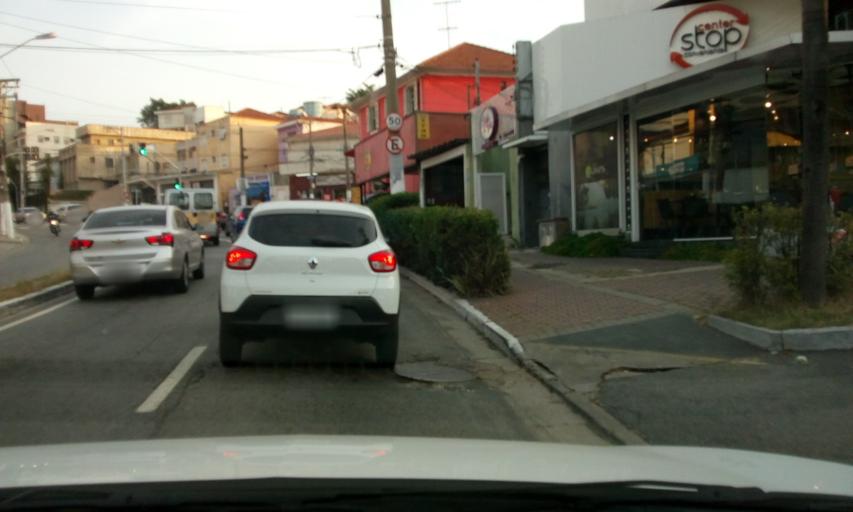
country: BR
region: Sao Paulo
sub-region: Sao Paulo
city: Sao Paulo
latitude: -23.5383
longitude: -46.6908
